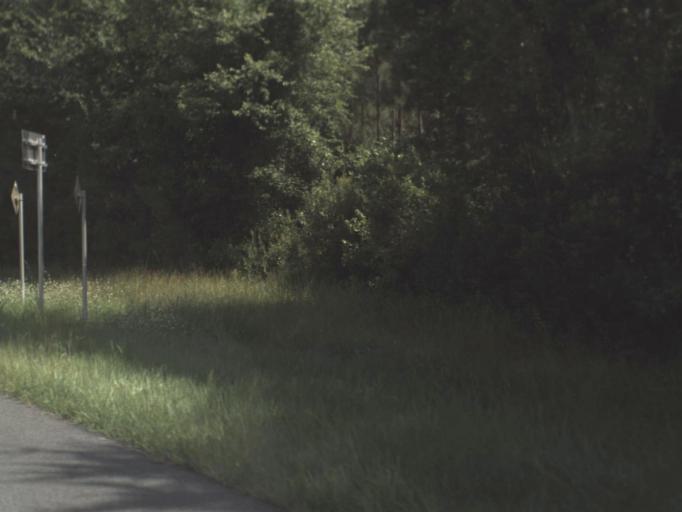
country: US
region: Florida
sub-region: Hamilton County
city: Jasper
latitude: 30.5962
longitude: -83.0106
